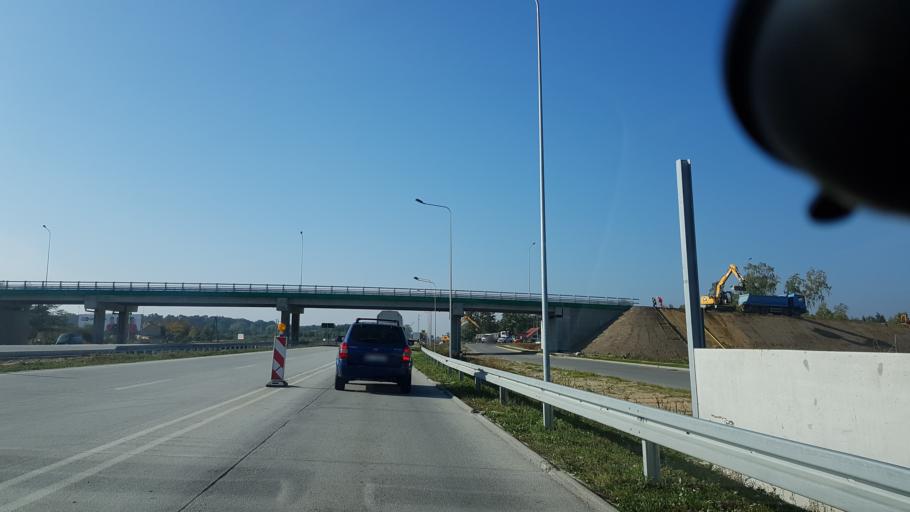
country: PL
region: Lodz Voivodeship
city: Zabia Wola
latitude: 52.0361
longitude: 20.6927
